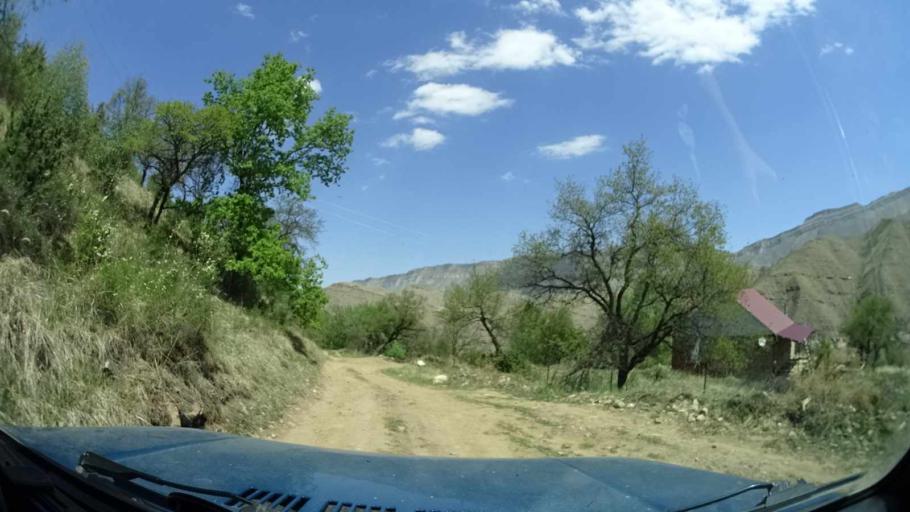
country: RU
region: Dagestan
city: Gunib
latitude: 42.3082
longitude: 47.0041
